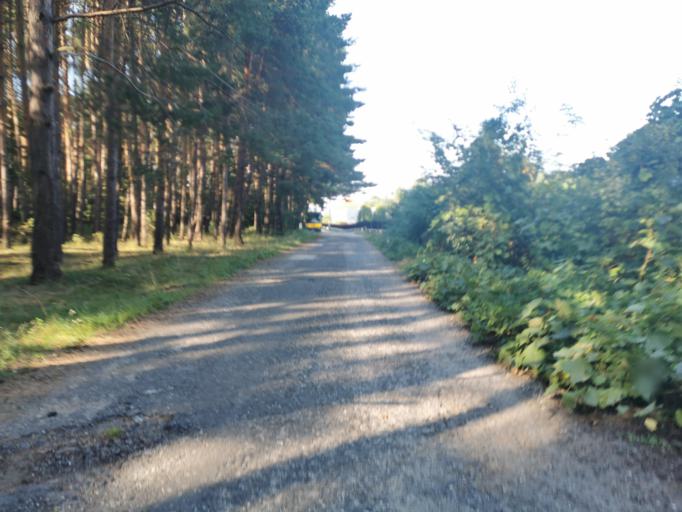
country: SK
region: Trnavsky
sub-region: Okres Senica
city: Senica
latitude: 48.6484
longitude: 17.2686
